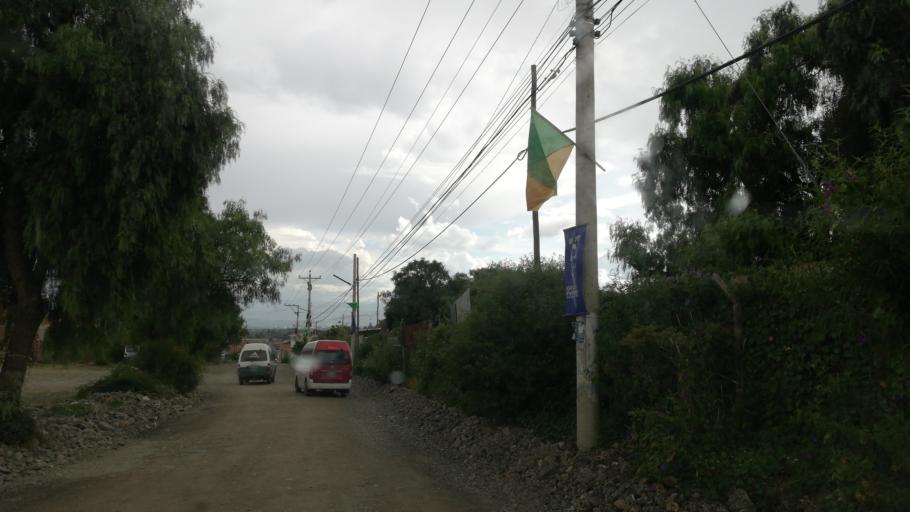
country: BO
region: Cochabamba
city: Cochabamba
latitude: -17.3410
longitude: -66.1996
